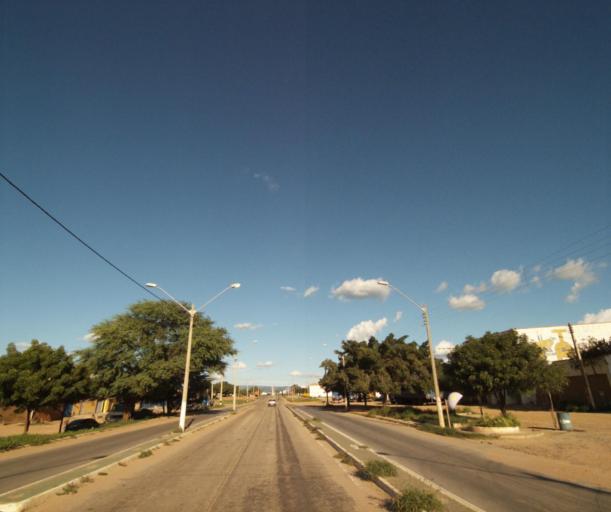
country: BR
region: Bahia
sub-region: Guanambi
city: Guanambi
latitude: -14.2105
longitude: -42.7879
